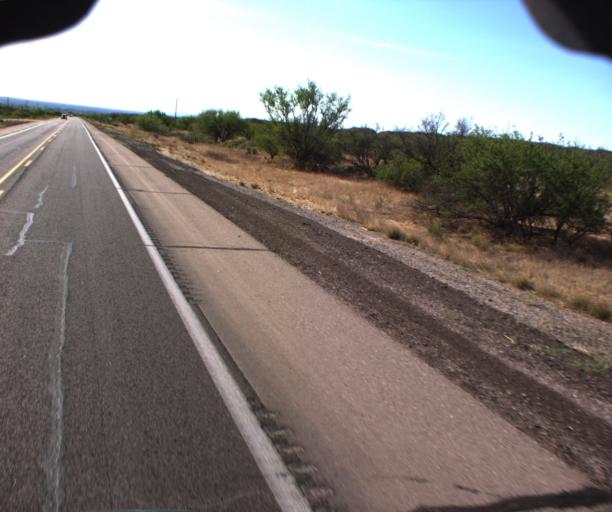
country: US
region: Arizona
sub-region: Cochise County
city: Benson
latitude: 31.9315
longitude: -110.2828
